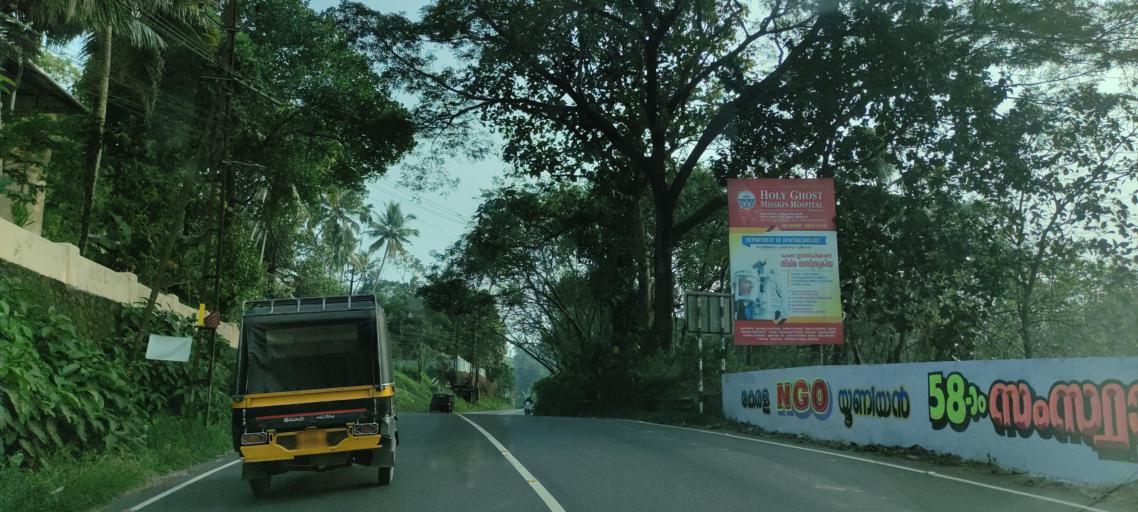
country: IN
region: Kerala
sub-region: Kottayam
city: Vaikam
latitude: 9.7638
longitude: 76.4928
